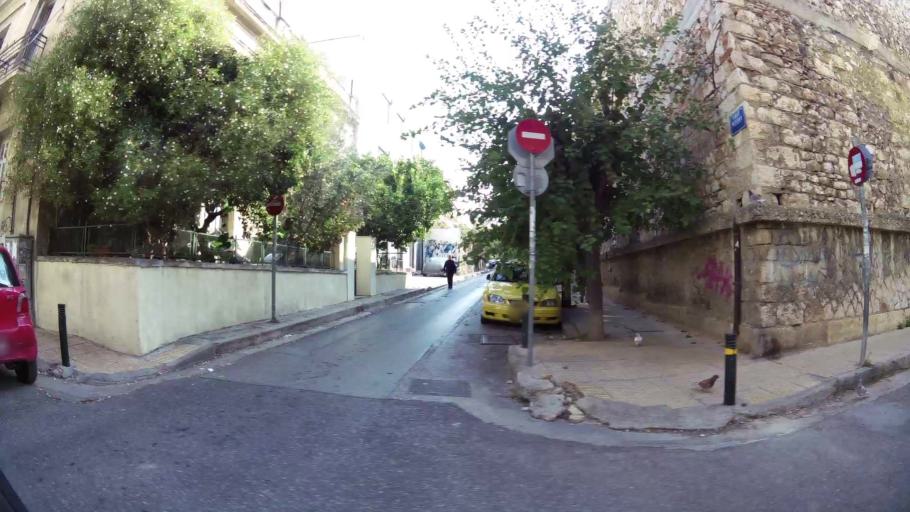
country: GR
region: Attica
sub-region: Nomarchia Athinas
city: Nea Chalkidona
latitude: 38.0179
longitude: 23.7366
